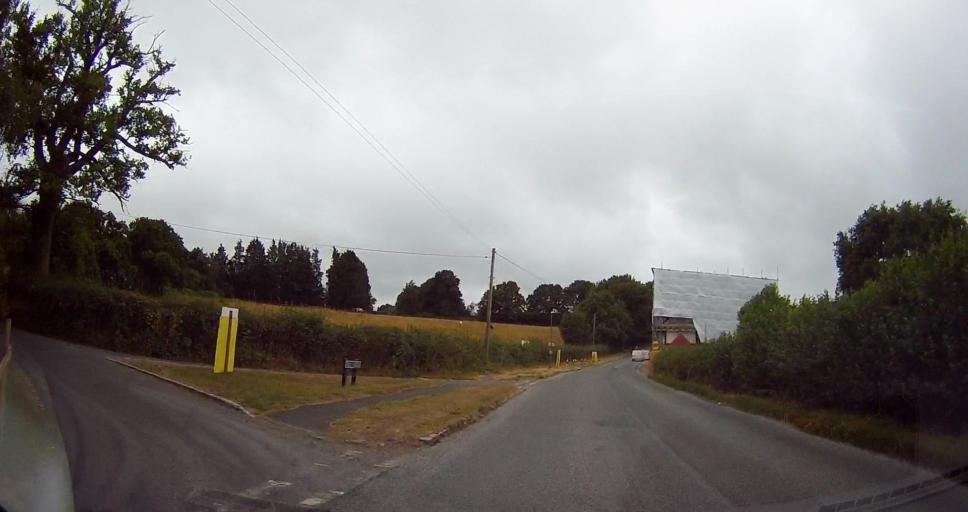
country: GB
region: England
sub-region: East Sussex
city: Wadhurst
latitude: 51.0723
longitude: 0.3446
